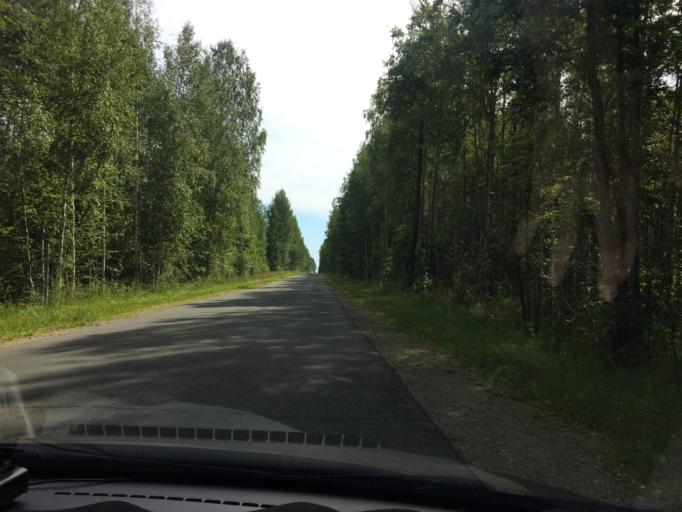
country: RU
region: Mariy-El
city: Surok
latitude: 56.5698
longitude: 48.2353
